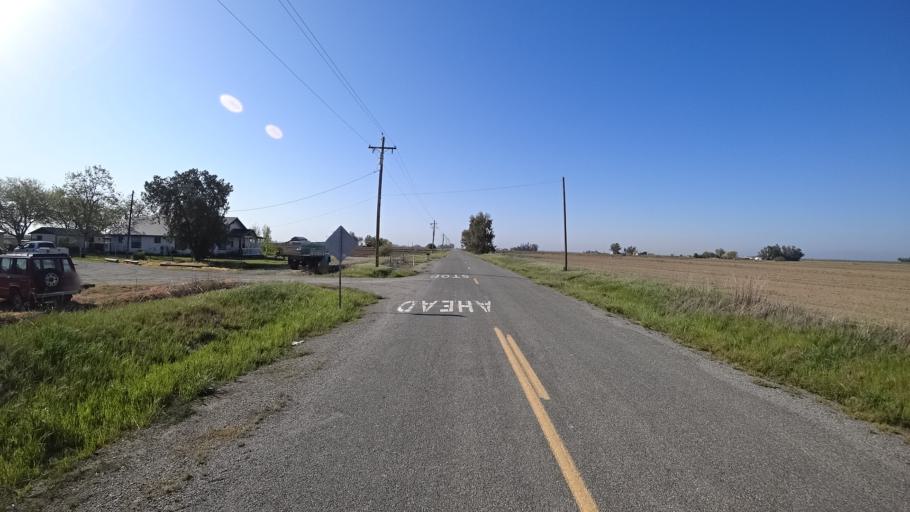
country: US
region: California
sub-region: Glenn County
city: Willows
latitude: 39.5808
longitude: -122.1075
